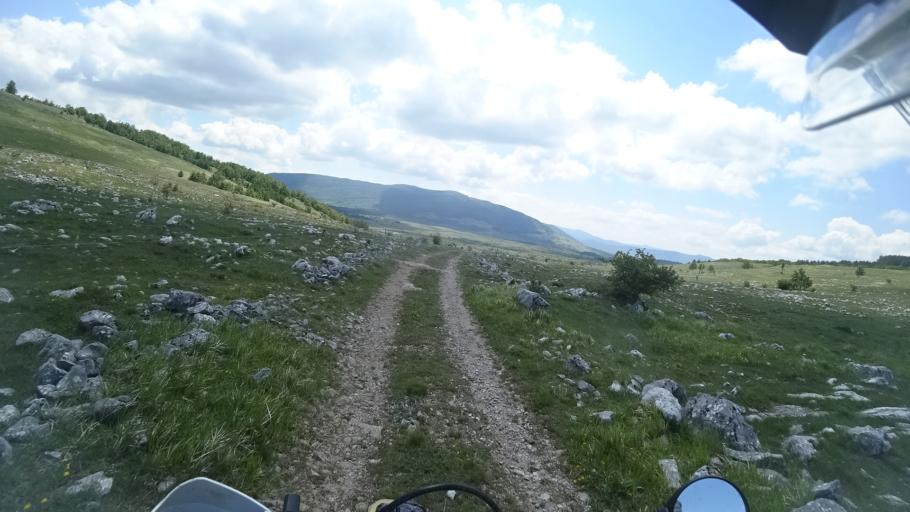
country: HR
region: Zadarska
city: Gracac
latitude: 44.3704
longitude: 15.9577
